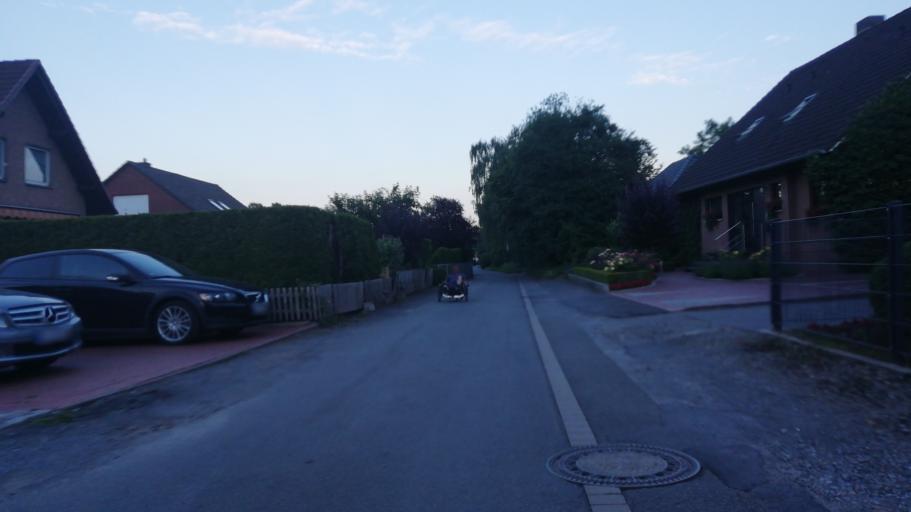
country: DE
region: North Rhine-Westphalia
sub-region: Regierungsbezirk Detmold
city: Minden
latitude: 52.2720
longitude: 8.8954
